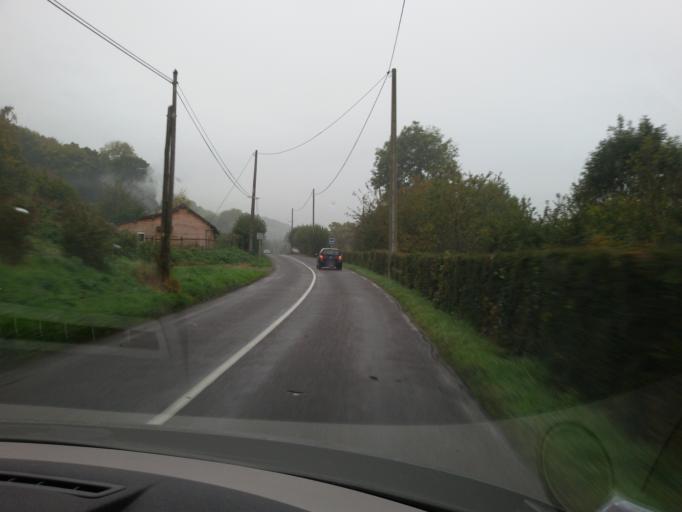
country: FR
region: Lower Normandy
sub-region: Departement du Calvados
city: Ablon
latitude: 49.4203
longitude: 0.3180
